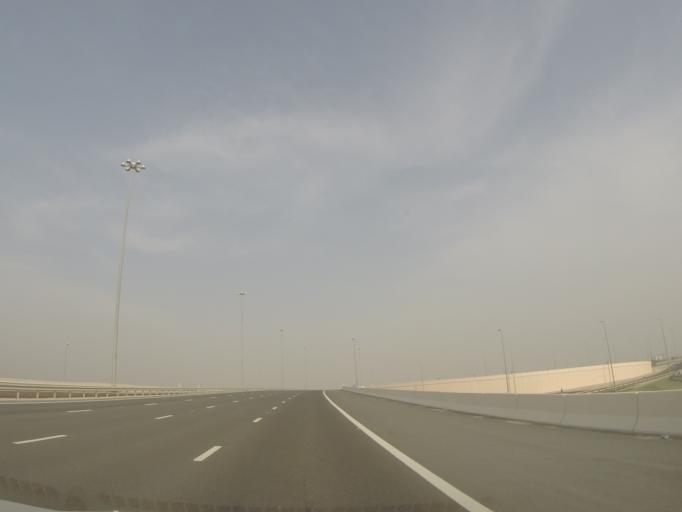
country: AE
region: Abu Dhabi
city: Abu Dhabi
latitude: 24.6963
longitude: 54.7754
